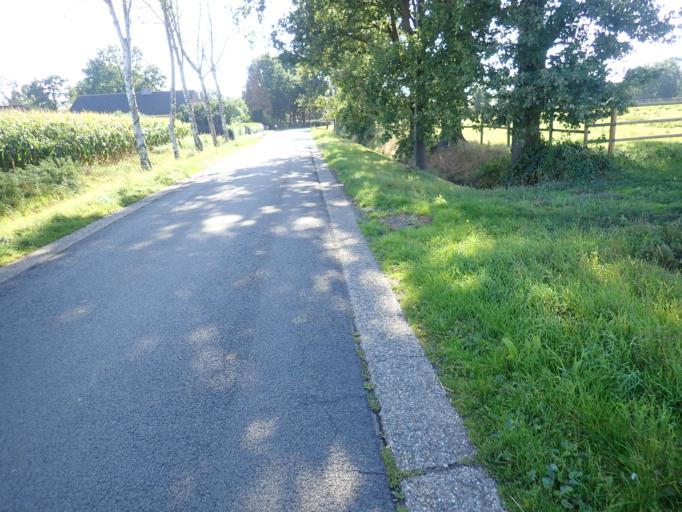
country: BE
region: Flanders
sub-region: Provincie Antwerpen
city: Herenthout
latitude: 51.1377
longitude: 4.7856
